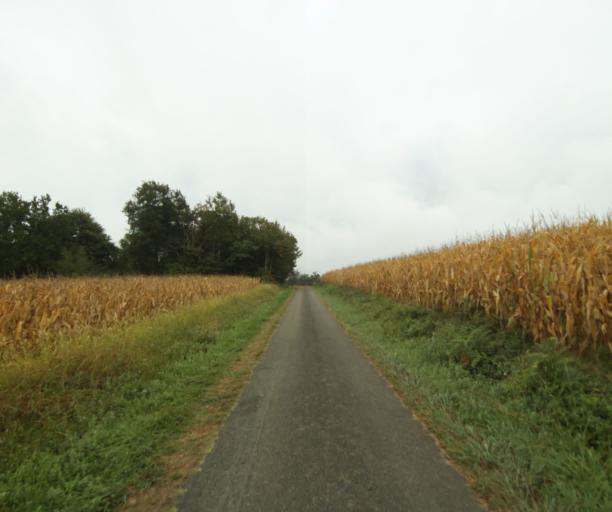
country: FR
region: Midi-Pyrenees
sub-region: Departement du Gers
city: Cazaubon
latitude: 43.9214
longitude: -0.1466
